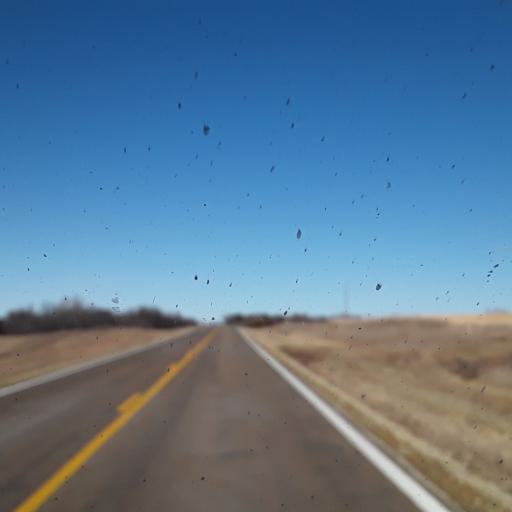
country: US
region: Kansas
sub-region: Mitchell County
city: Beloit
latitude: 39.3104
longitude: -98.1164
